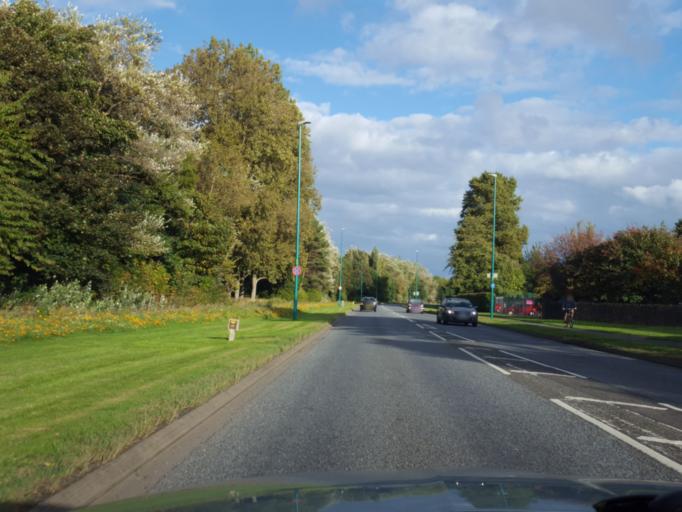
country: GB
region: Scotland
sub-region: Dundee City
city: Dundee
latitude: 56.4545
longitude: -3.0085
